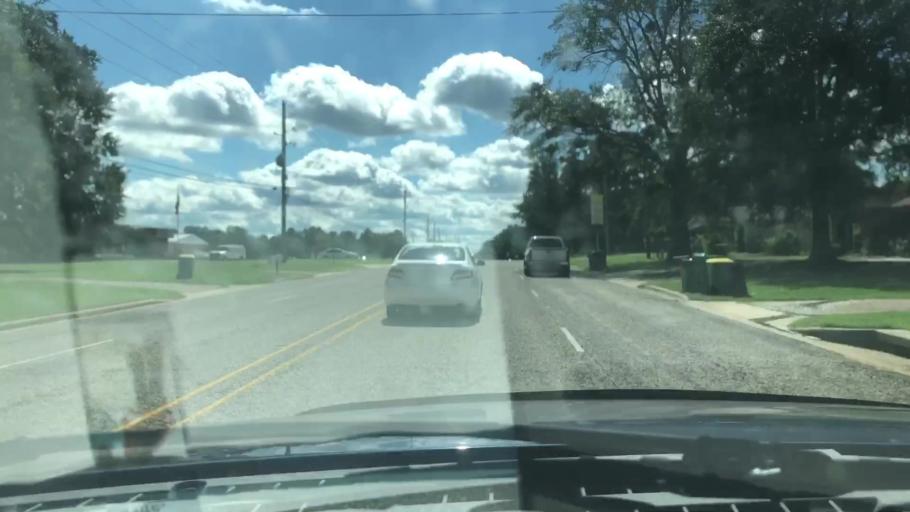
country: US
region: Texas
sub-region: Bowie County
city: Wake Village
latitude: 33.3936
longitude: -94.0922
